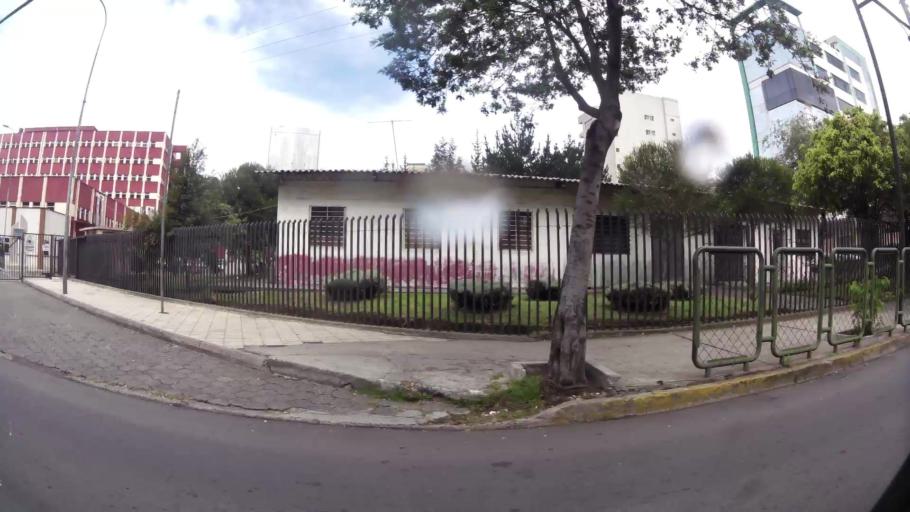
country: EC
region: Pichincha
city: Quito
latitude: -0.2029
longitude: -78.4870
